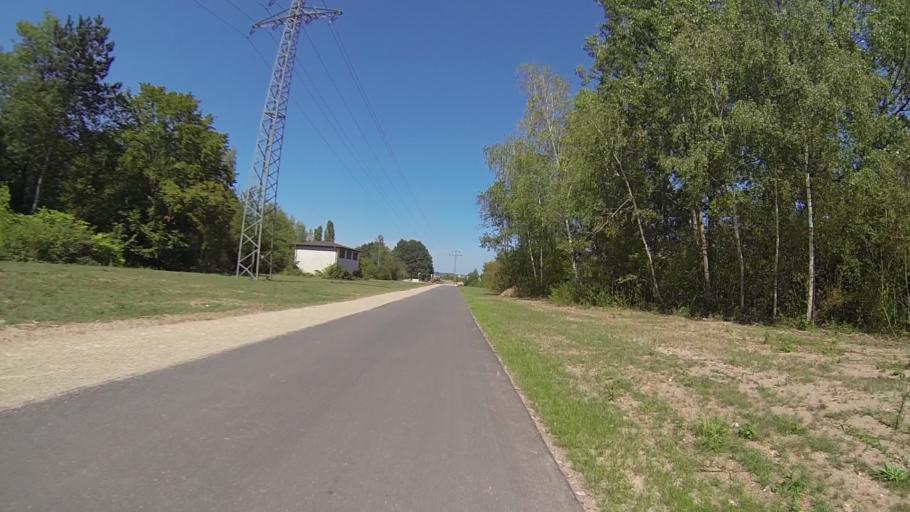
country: DE
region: Rheinland-Pfalz
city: Trier
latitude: 49.7265
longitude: 6.6164
